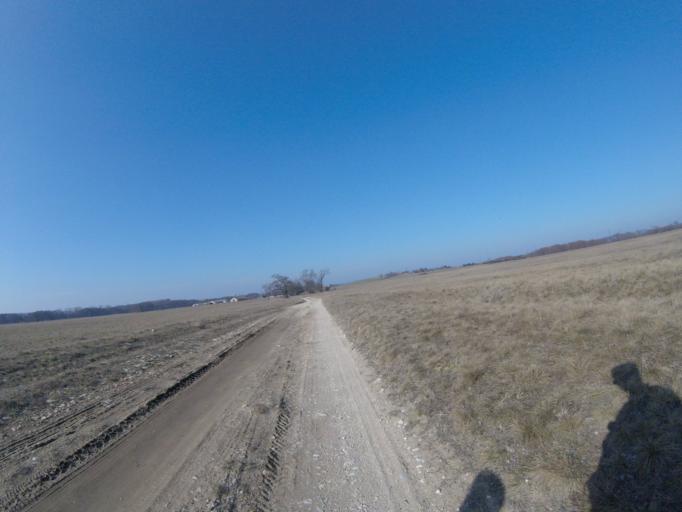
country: HU
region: Komarom-Esztergom
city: Oroszlany
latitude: 47.4667
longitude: 18.3413
